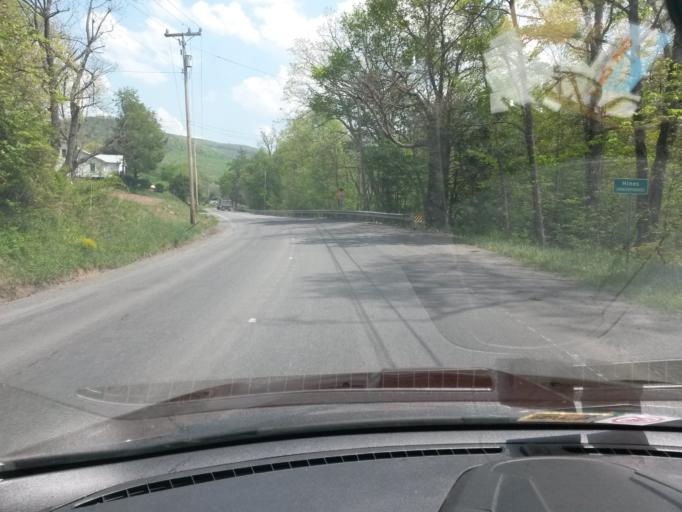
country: US
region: West Virginia
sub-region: Greenbrier County
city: Rainelle
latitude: 37.9862
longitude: -80.7256
